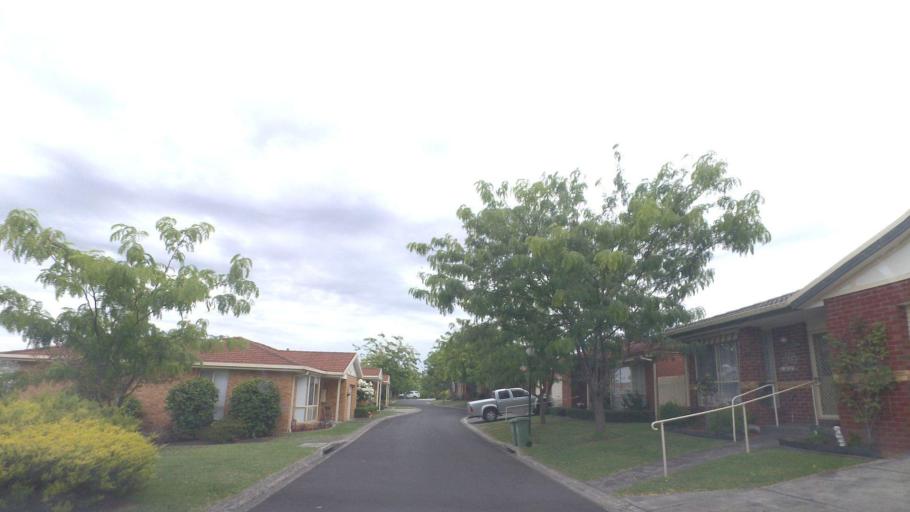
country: AU
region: Victoria
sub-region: Yarra Ranges
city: Lilydale
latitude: -37.7563
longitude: 145.3706
